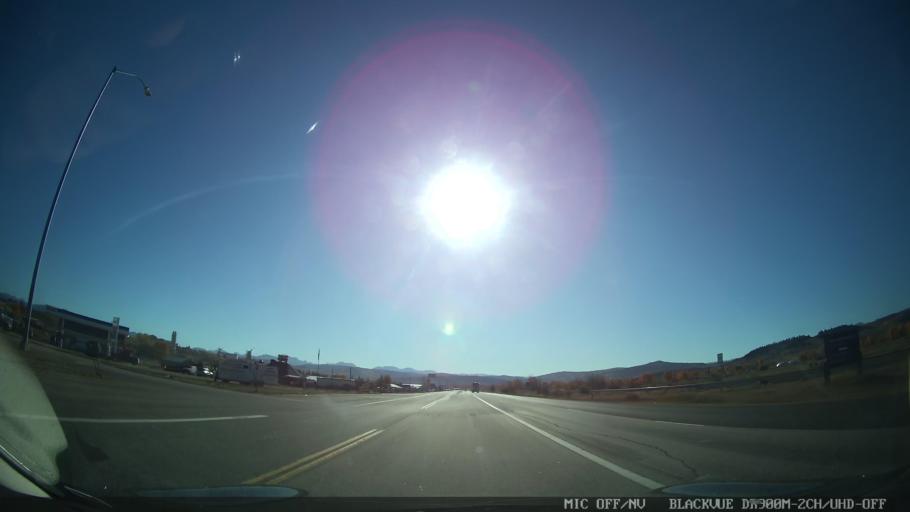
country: US
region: Colorado
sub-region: Grand County
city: Granby
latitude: 40.0904
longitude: -105.9583
